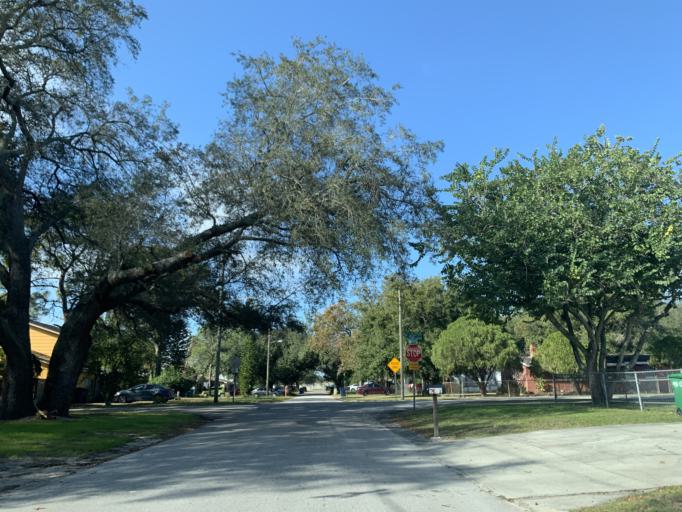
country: US
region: Florida
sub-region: Hillsborough County
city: Temple Terrace
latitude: 28.0362
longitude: -82.4117
